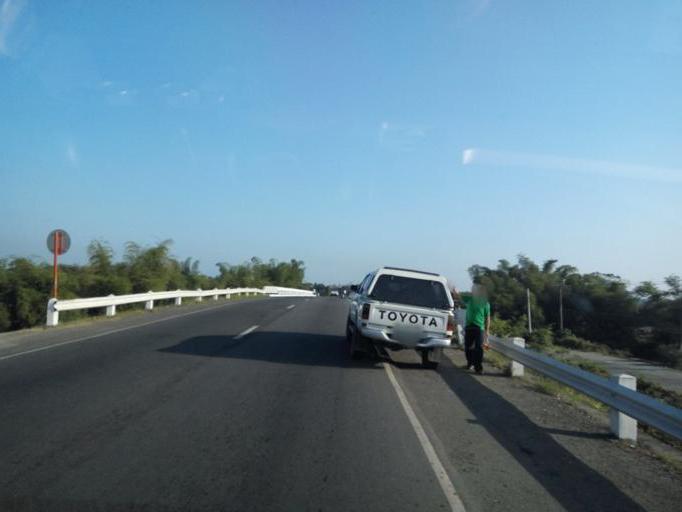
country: PH
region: Cagayan Valley
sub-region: Province of Cagayan
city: Gammad
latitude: 17.7295
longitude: 121.7390
